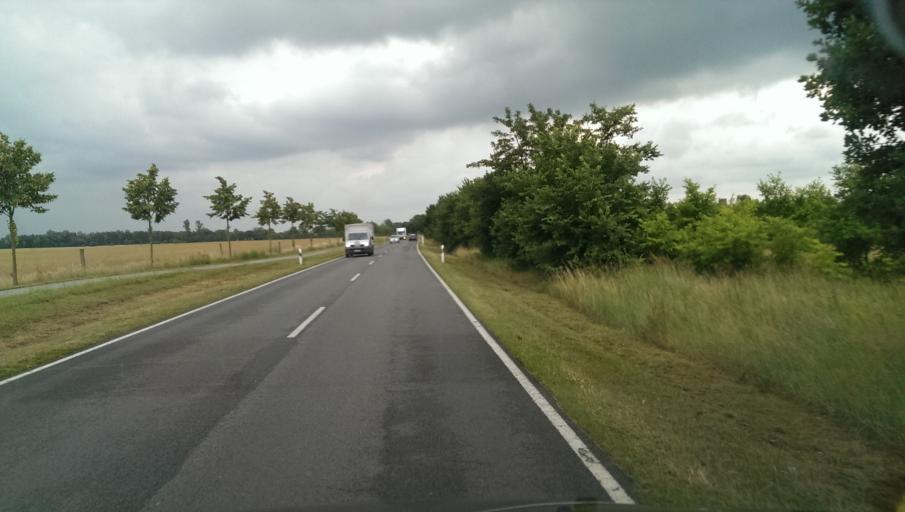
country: DE
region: Brandenburg
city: Rathenow
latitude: 52.6433
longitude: 12.3304
